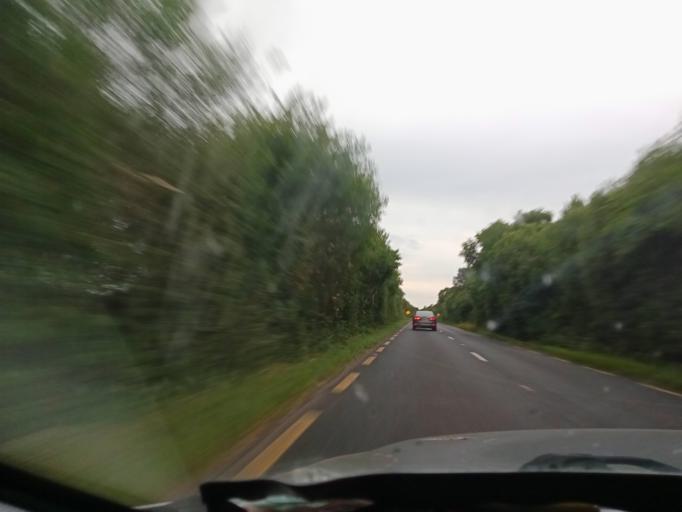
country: IE
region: Leinster
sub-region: Laois
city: Mountmellick
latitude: 53.0718
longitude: -7.3285
